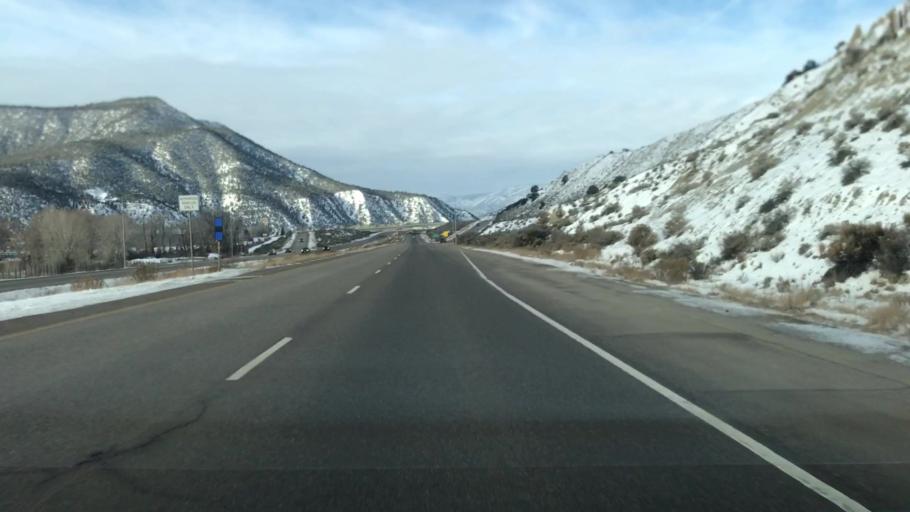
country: US
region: Colorado
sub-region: Eagle County
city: Gypsum
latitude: 39.6533
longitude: -106.9469
